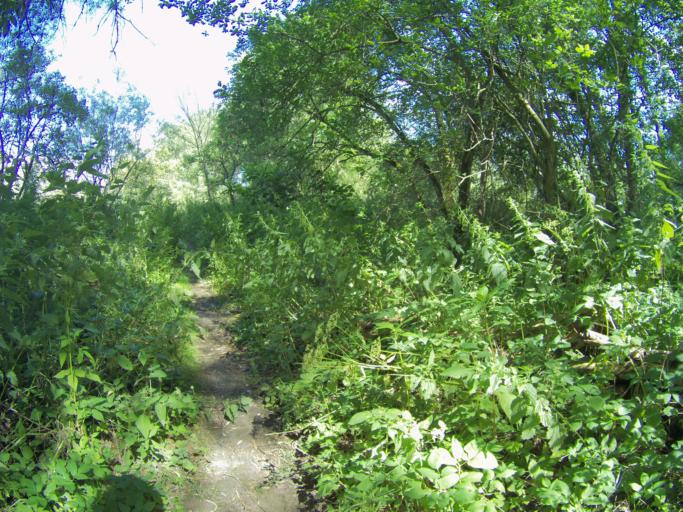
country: DE
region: Bavaria
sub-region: Upper Bavaria
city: Langenbach
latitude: 48.4058
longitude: 11.8293
